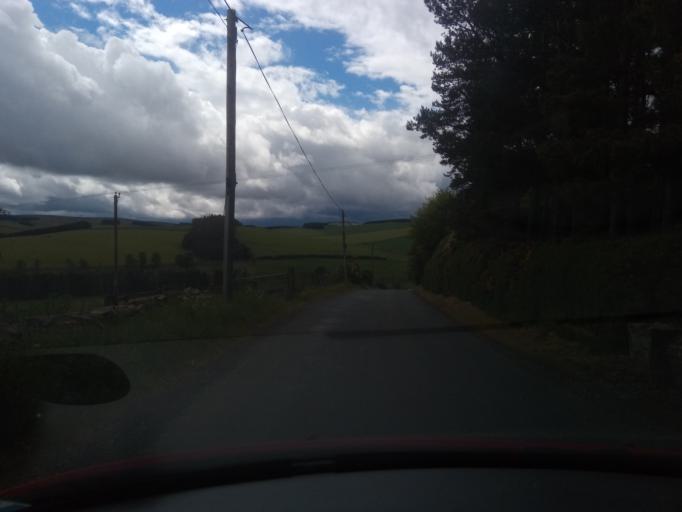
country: GB
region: Scotland
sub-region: Fife
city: Pathhead
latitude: 55.7592
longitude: -2.9199
